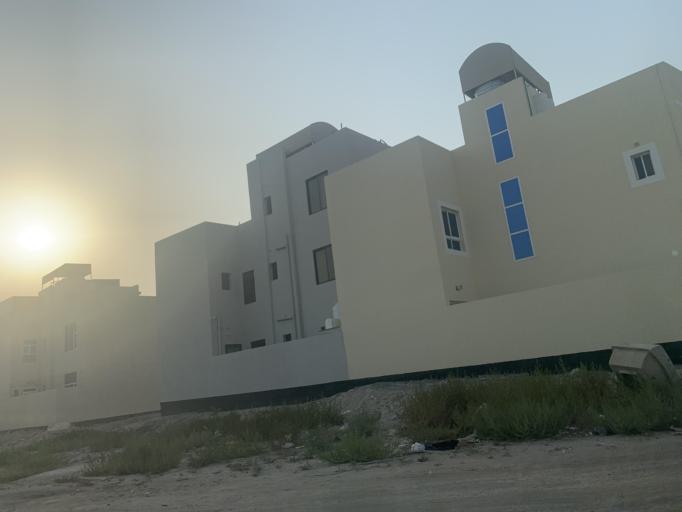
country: BH
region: Manama
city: Jidd Hafs
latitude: 26.2187
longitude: 50.5194
